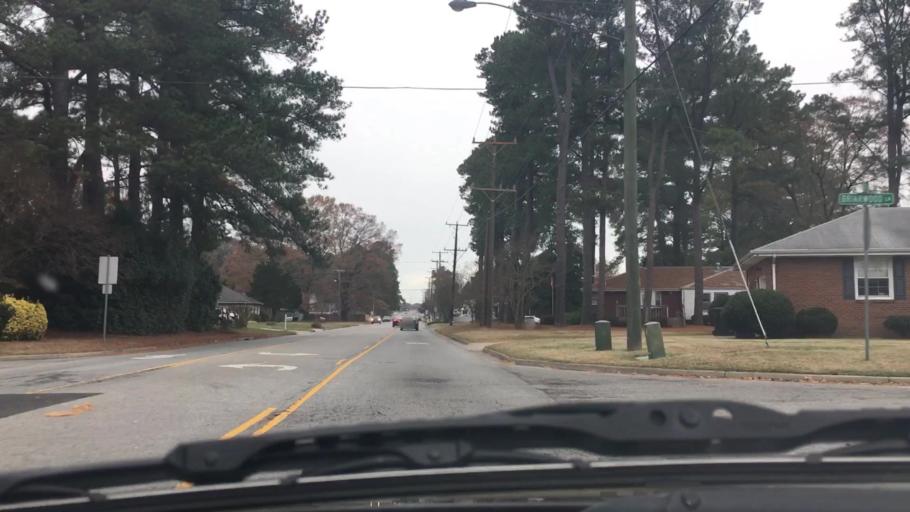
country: US
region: Virginia
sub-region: City of Portsmouth
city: Portsmouth Heights
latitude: 36.8636
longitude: -76.3770
